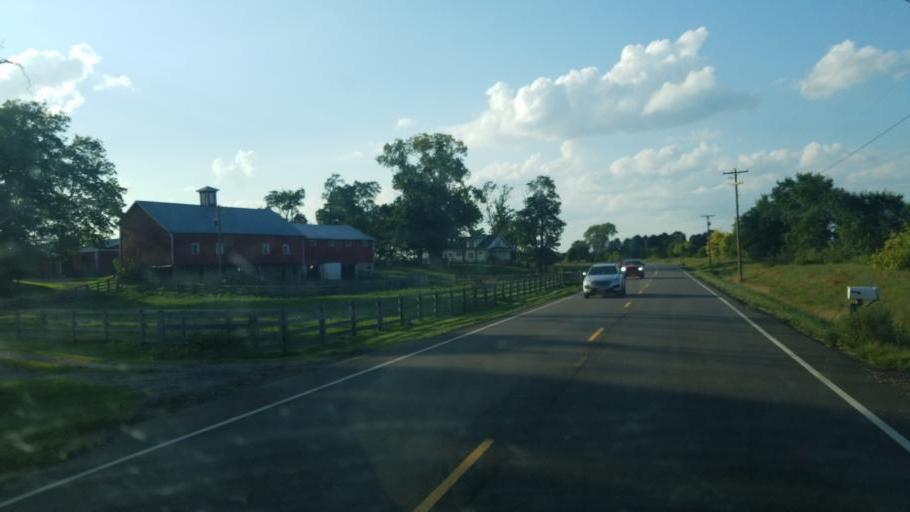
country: US
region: Ohio
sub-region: Knox County
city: Mount Vernon
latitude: 40.4281
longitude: -82.5099
